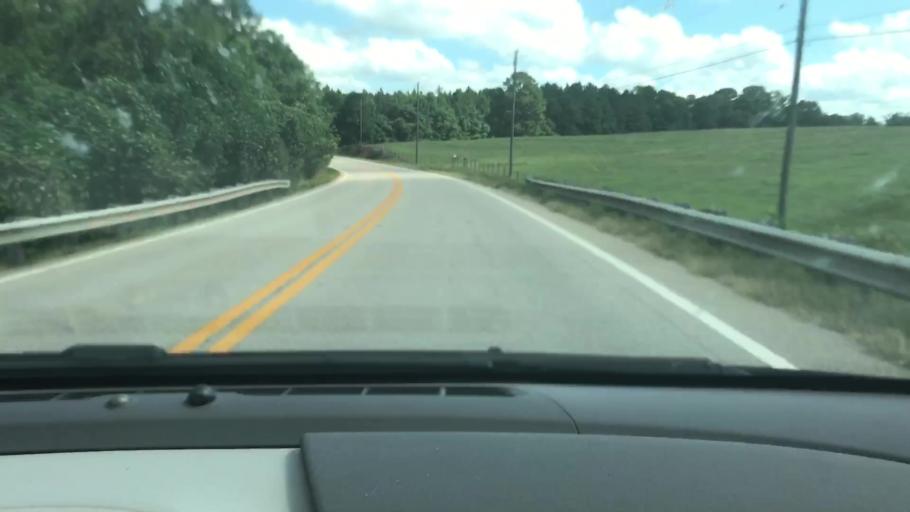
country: US
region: Georgia
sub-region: Troup County
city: La Grange
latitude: 32.9037
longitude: -85.0249
